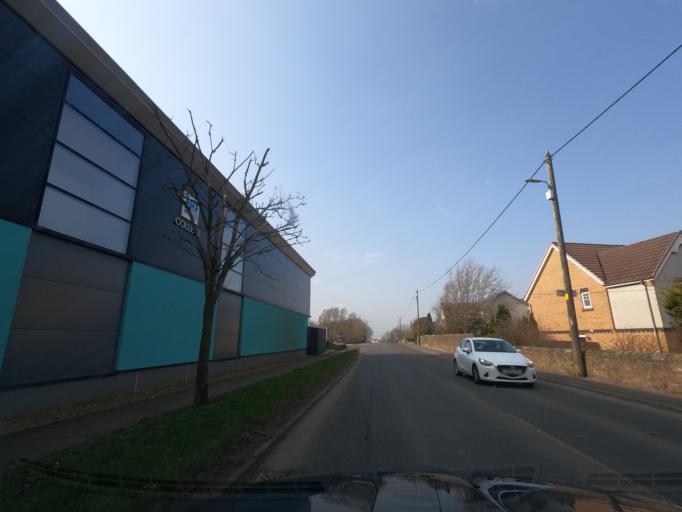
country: GB
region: Scotland
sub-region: Falkirk
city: Polmont
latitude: 55.9831
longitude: -3.7266
